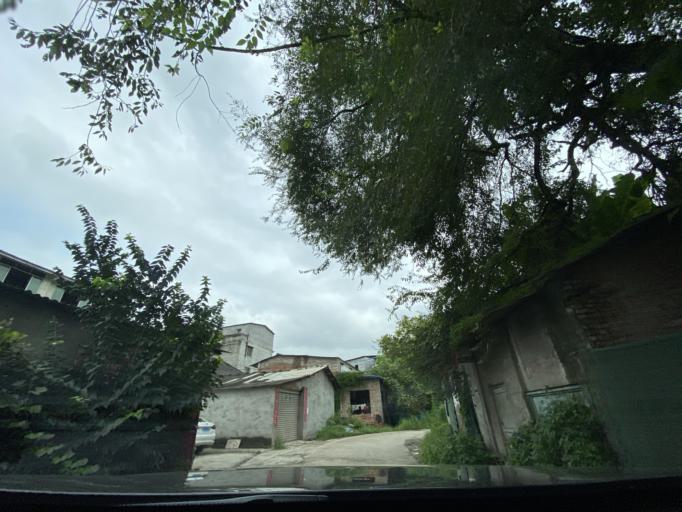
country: CN
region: Sichuan
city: Jiancheng
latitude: 30.3984
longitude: 104.5628
